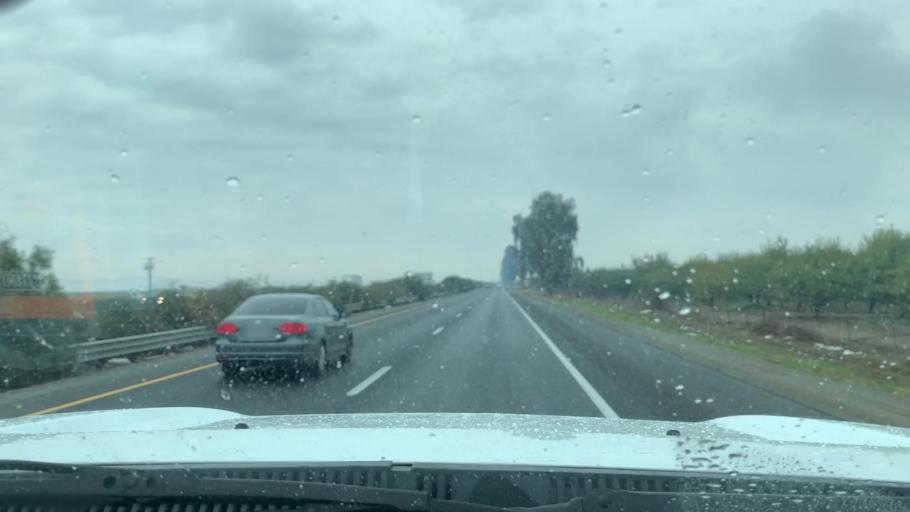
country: US
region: California
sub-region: Kern County
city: Delano
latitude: 35.7960
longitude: -119.2536
